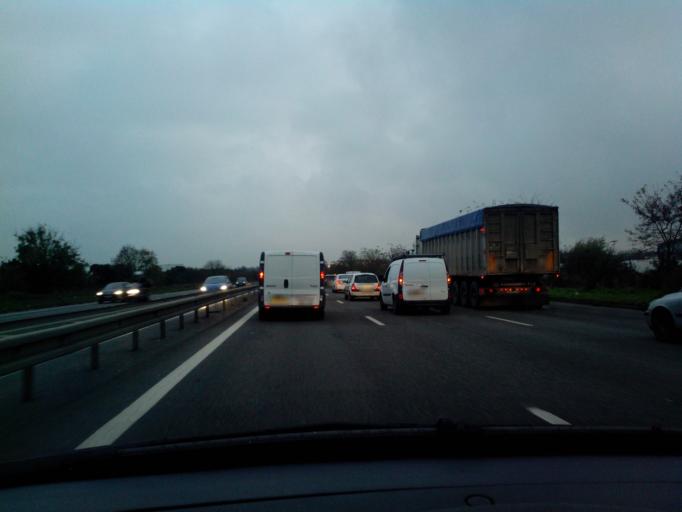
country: FR
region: Ile-de-France
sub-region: Departement de l'Essonne
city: Chilly-Mazarin
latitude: 48.7207
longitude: 2.3111
